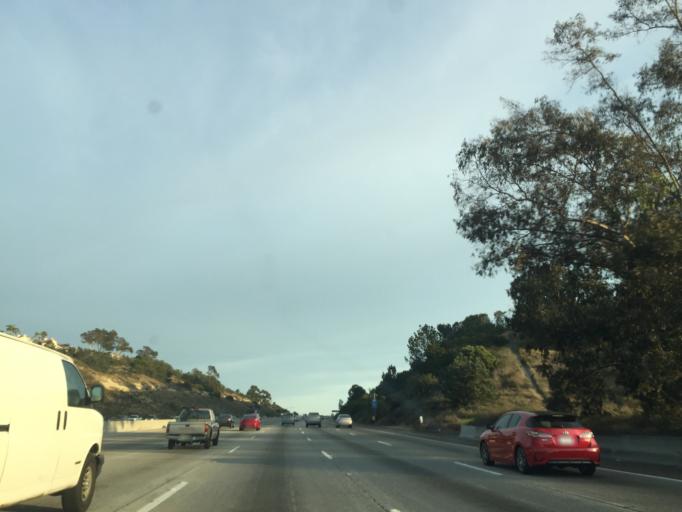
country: US
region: California
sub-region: San Diego County
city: Del Mar
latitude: 32.9608
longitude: -117.2461
